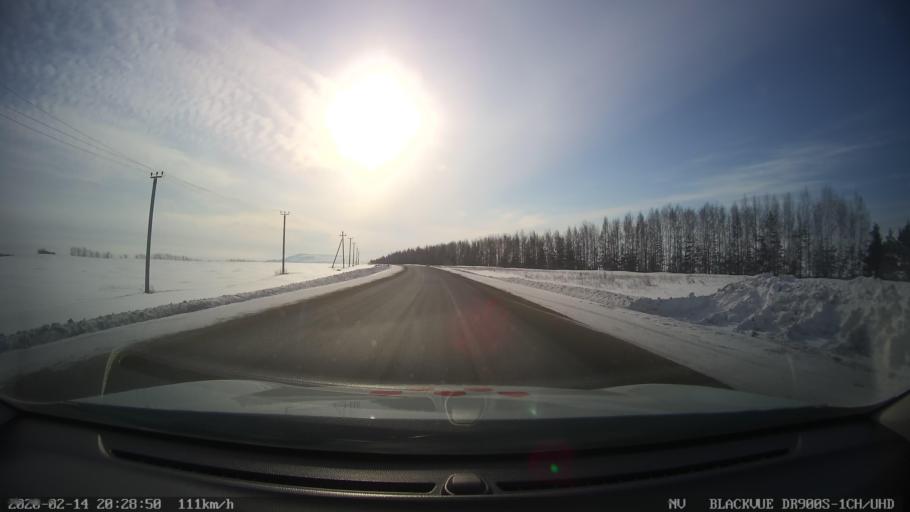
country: RU
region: Tatarstan
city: Stolbishchi
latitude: 55.4573
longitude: 48.9776
